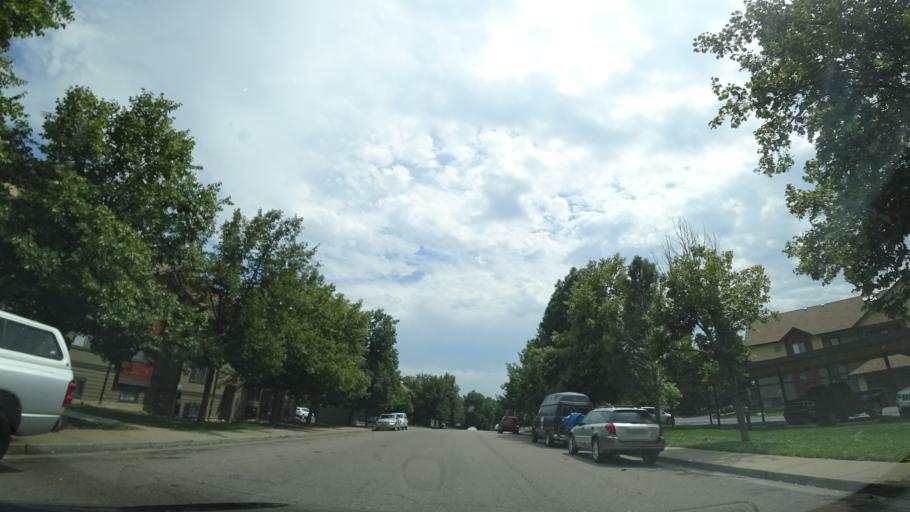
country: US
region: Colorado
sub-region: Jefferson County
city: Lakewood
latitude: 39.7030
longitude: -105.0735
